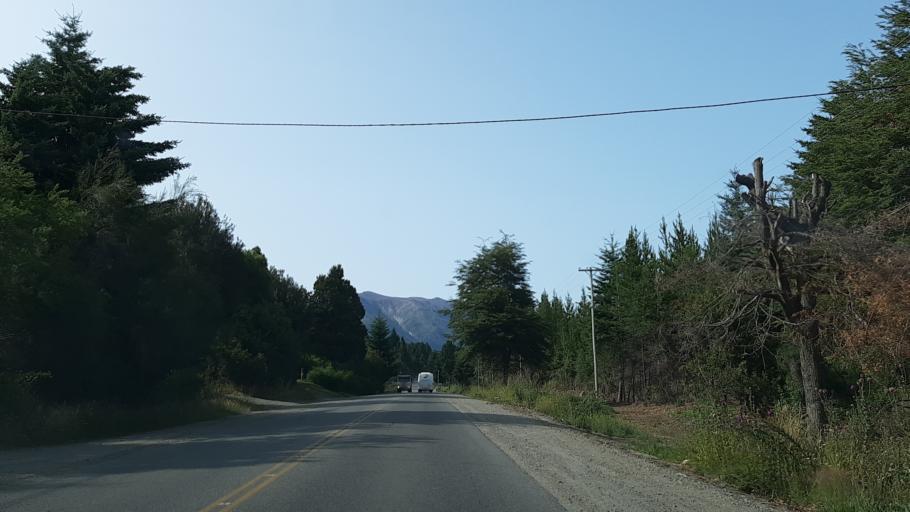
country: AR
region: Rio Negro
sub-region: Departamento de Bariloche
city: San Carlos de Bariloche
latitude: -41.1511
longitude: -71.4088
